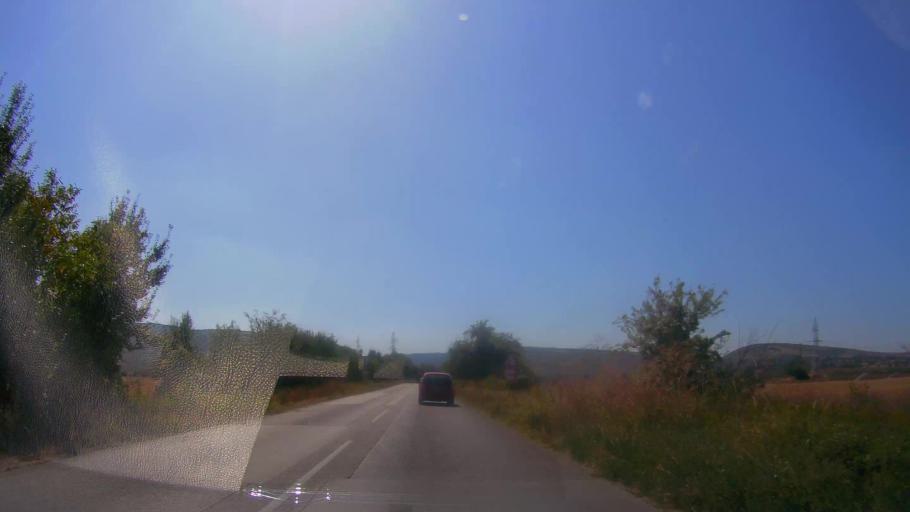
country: BG
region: Veliko Turnovo
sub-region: Obshtina Gorna Oryakhovitsa
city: Purvomaytsi
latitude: 43.1551
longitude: 25.6186
